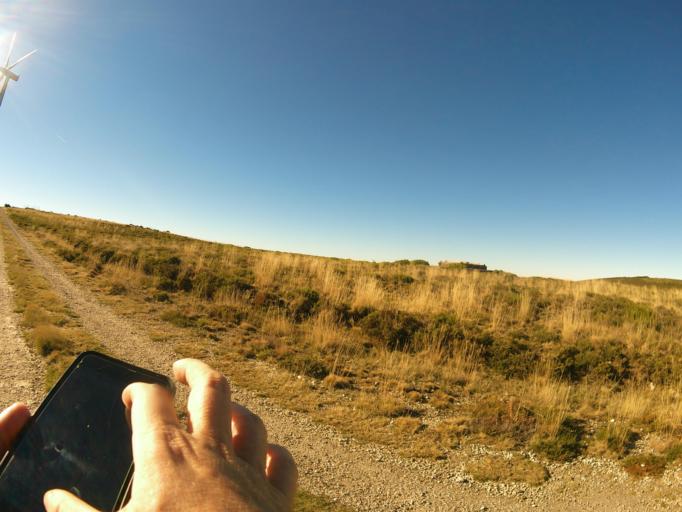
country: PT
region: Vila Real
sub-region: Mesao Frio
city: Mesao Frio
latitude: 41.2328
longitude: -7.9062
